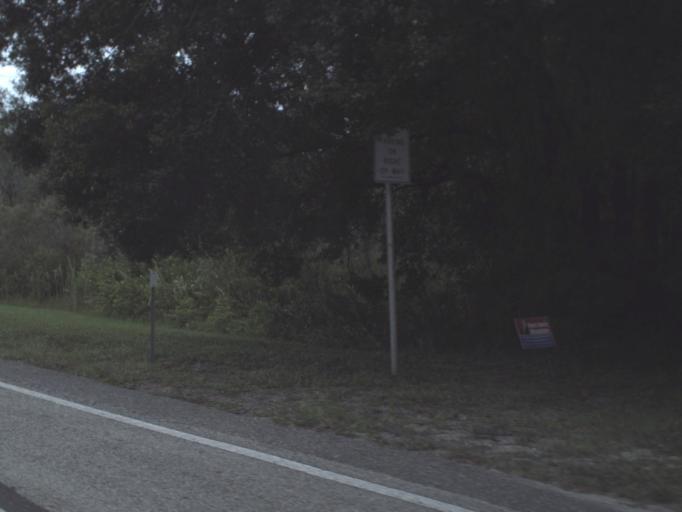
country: US
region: Florida
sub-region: Sarasota County
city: North Port
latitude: 27.0960
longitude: -82.1555
